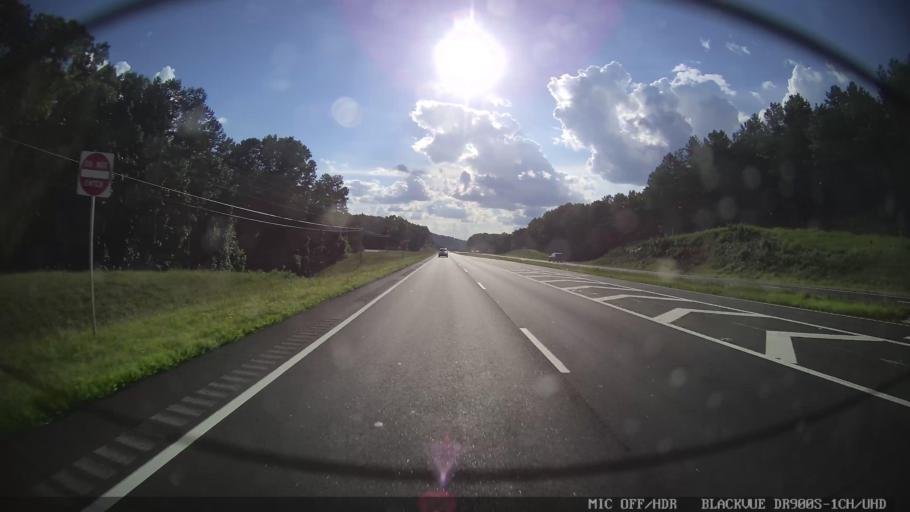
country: US
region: Georgia
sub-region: Floyd County
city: Rome
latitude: 34.2143
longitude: -85.1073
